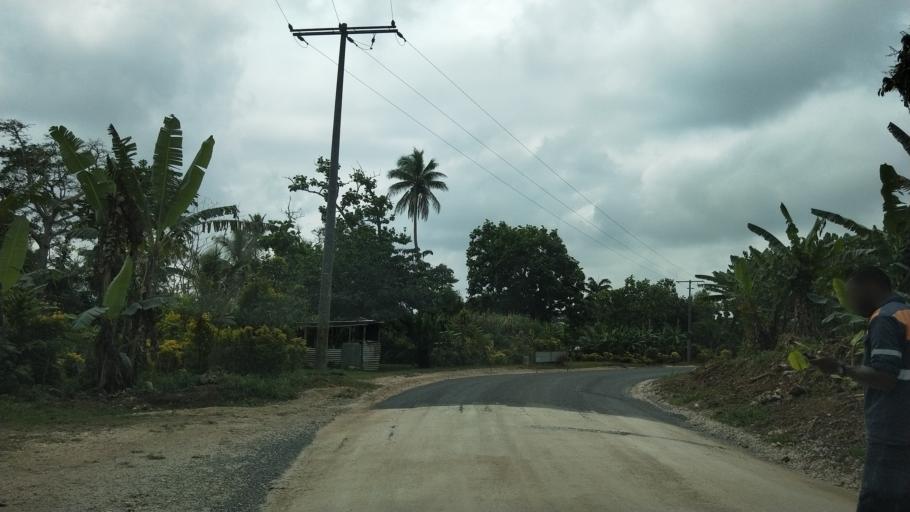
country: VU
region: Shefa
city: Port-Vila
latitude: -17.7789
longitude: 168.3630
